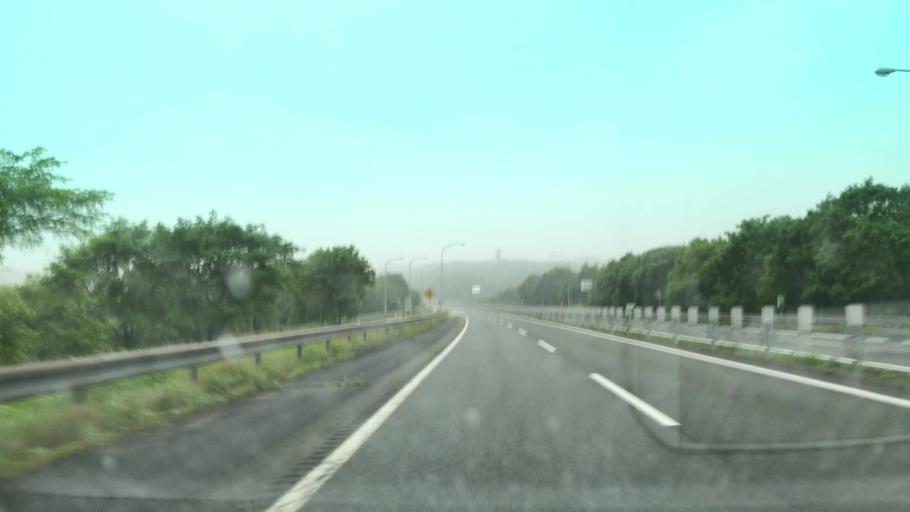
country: JP
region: Hokkaido
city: Tomakomai
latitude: 42.6329
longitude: 141.4902
